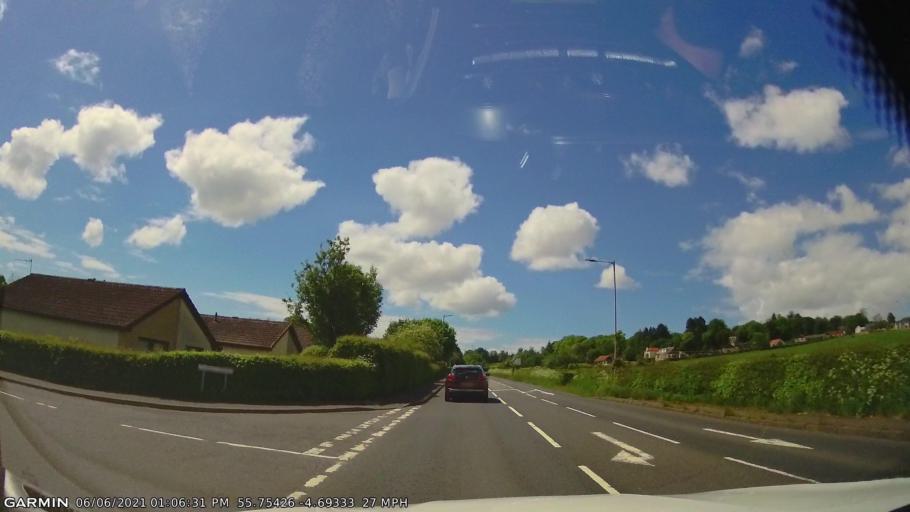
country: GB
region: Scotland
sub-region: North Ayrshire
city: Kilbirnie
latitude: 55.7543
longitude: -4.6931
